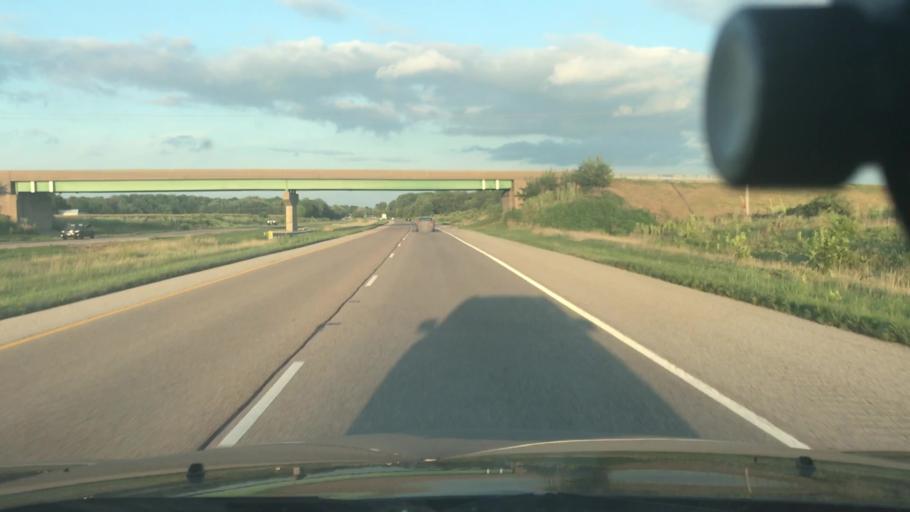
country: US
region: Illinois
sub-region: Clinton County
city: Albers
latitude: 38.5118
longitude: -89.6503
